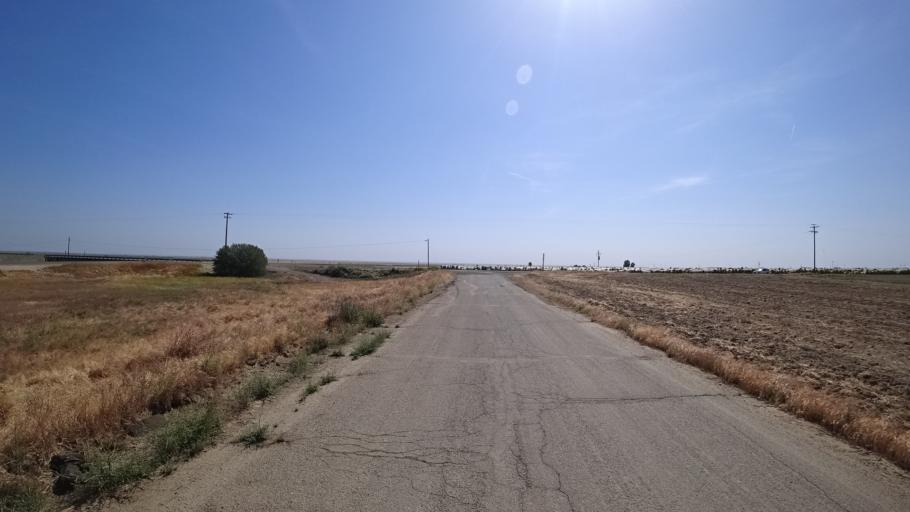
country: US
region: California
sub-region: Kings County
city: Kettleman City
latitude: 36.0470
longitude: -120.0045
